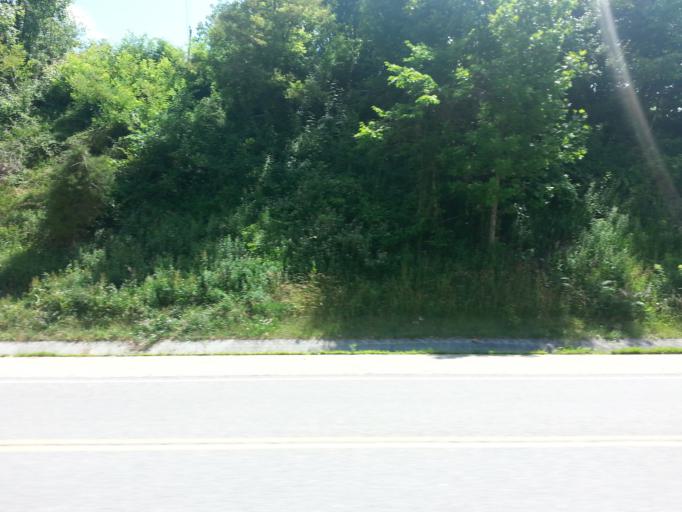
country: US
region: Virginia
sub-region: Lee County
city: Dryden
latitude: 36.7182
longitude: -82.9112
